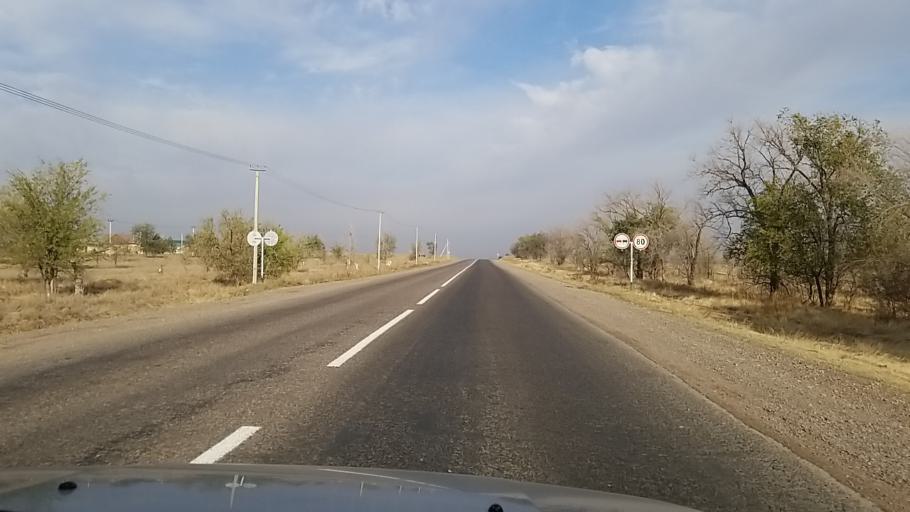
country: KZ
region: Almaty Oblysy
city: Burunday
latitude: 43.4840
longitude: 76.6740
